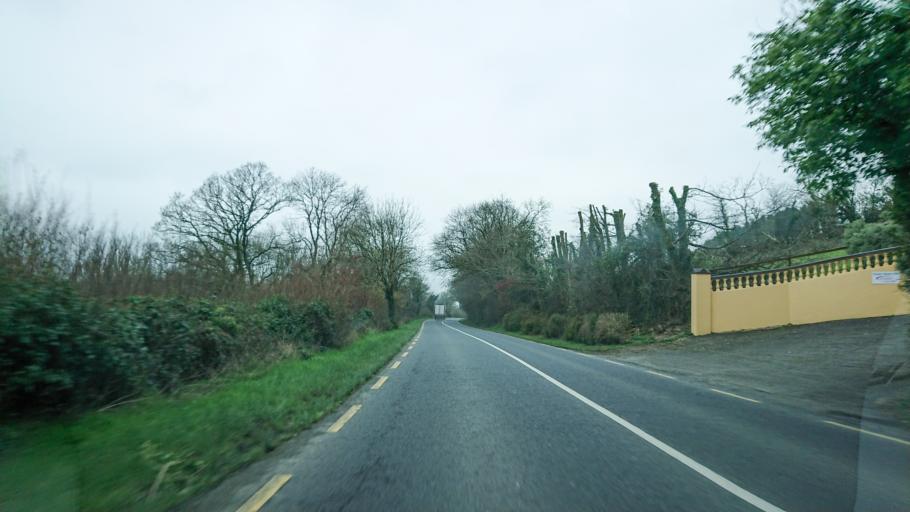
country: IE
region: Munster
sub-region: County Cork
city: Bandon
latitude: 51.7465
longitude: -8.7766
